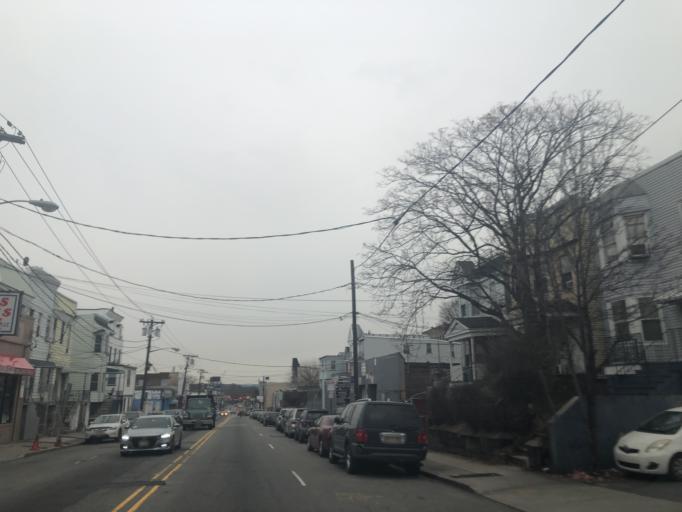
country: US
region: New Jersey
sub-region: Hudson County
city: Jersey City
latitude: 40.7199
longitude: -74.0790
